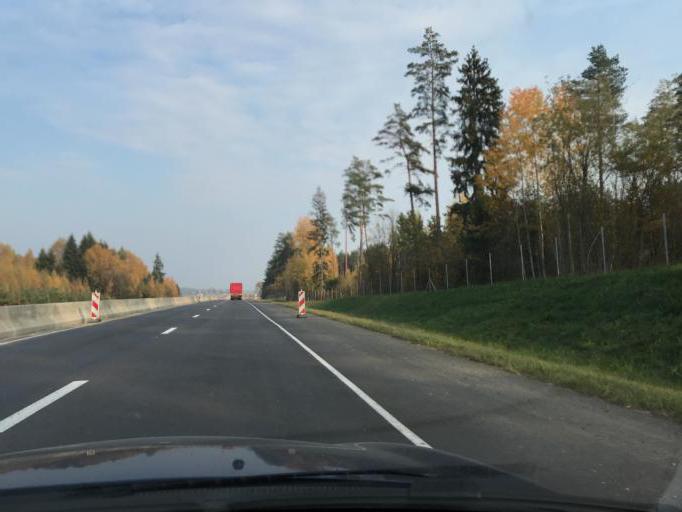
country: BY
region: Grodnenskaya
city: Shchuchin
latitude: 53.7051
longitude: 24.9211
